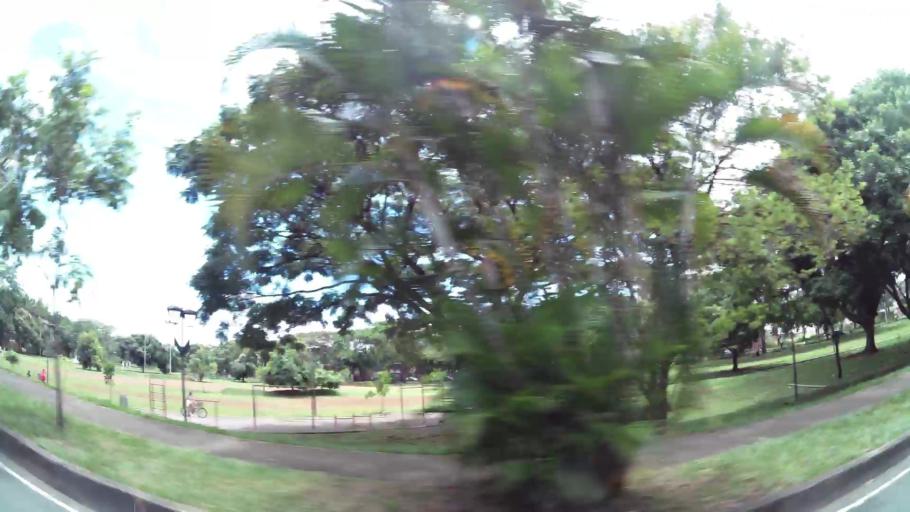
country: CO
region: Valle del Cauca
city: Cali
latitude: 3.3862
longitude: -76.5326
